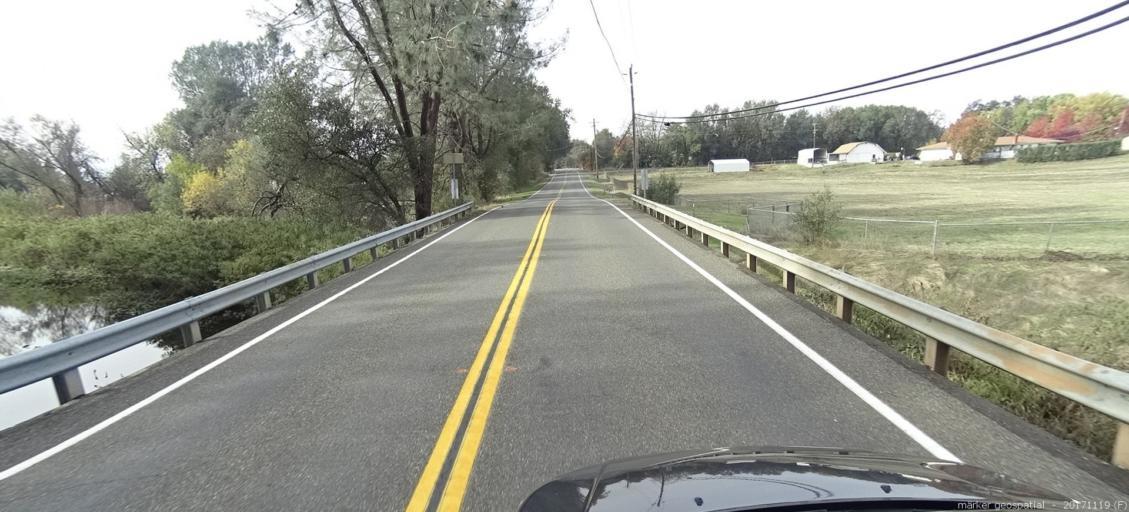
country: US
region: California
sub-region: Shasta County
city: Anderson
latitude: 40.4984
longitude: -122.3157
